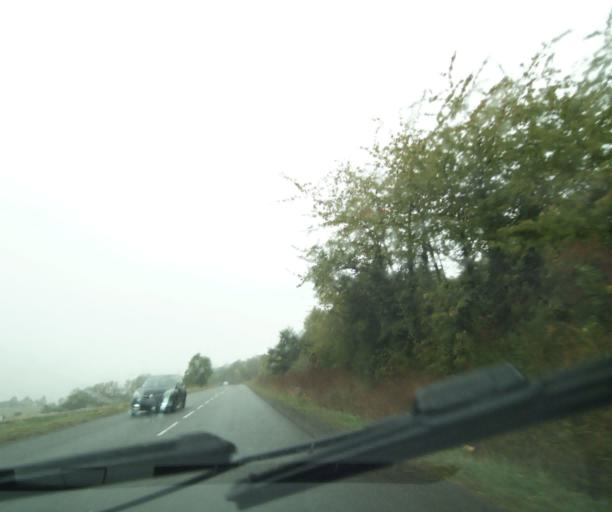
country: FR
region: Auvergne
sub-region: Departement du Puy-de-Dome
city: Chateaugay
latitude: 45.8467
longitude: 3.0827
